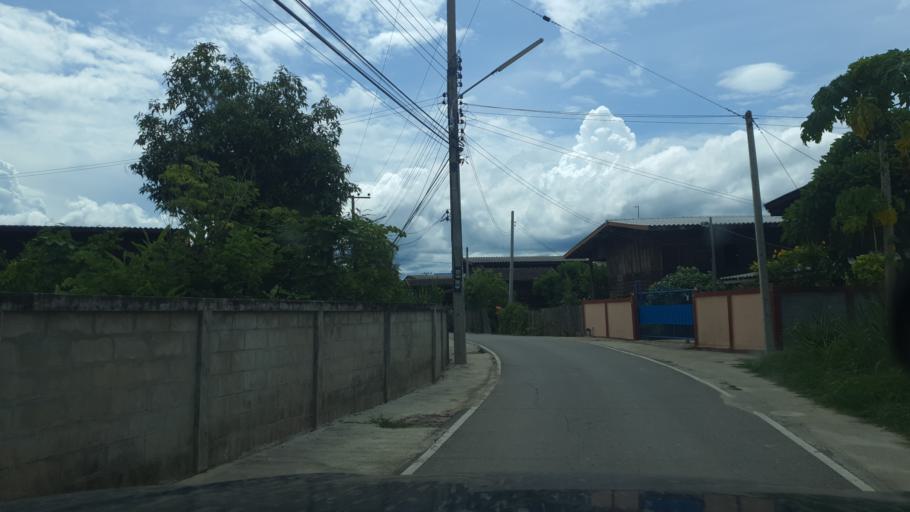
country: TH
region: Lampang
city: Sop Prap
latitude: 17.8832
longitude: 99.3819
